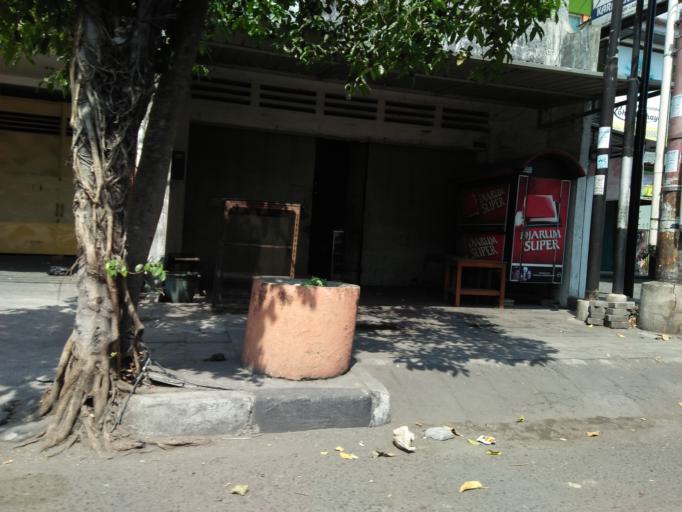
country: ID
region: Daerah Istimewa Yogyakarta
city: Kasihan
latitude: -7.8157
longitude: 110.3560
